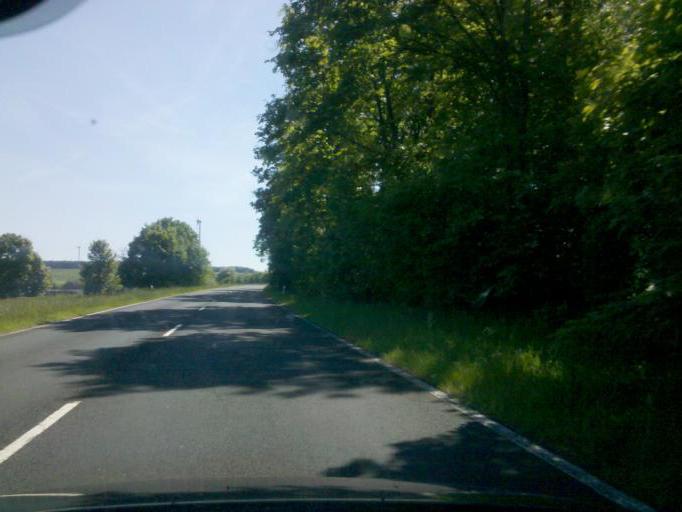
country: DE
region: Rheinland-Pfalz
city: Rehe
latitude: 50.6639
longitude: 8.1330
